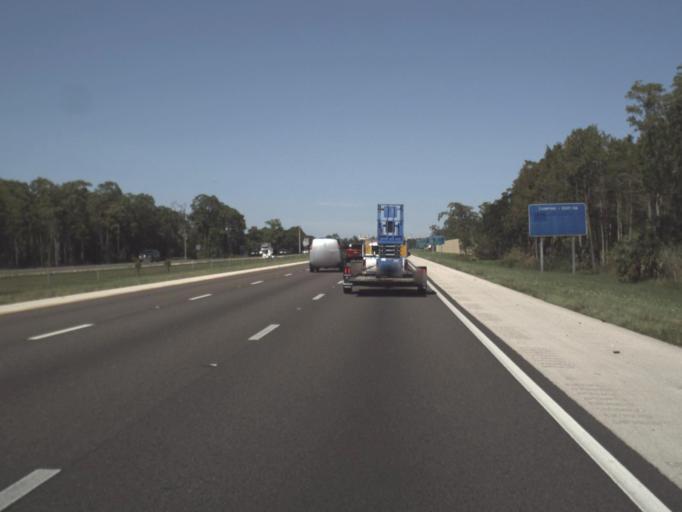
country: US
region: Florida
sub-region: Lee County
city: Bonita Springs
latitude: 26.3139
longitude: -81.7449
